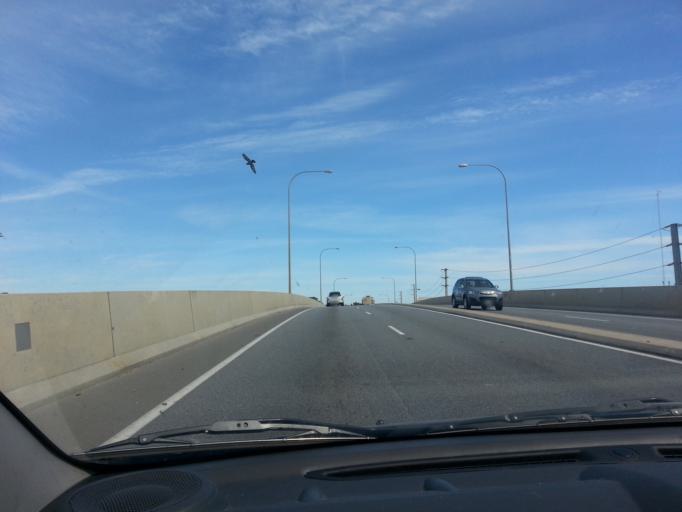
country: AU
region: South Australia
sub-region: Port Adelaide Enfield
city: Alberton
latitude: -34.8384
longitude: 138.5225
